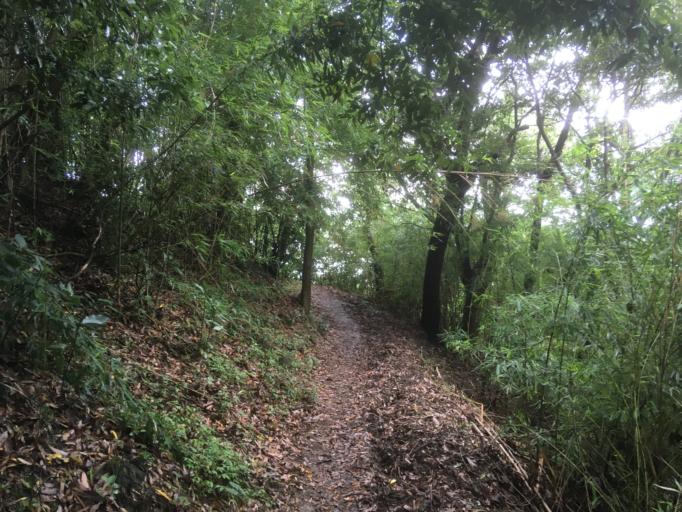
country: JP
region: Nara
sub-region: Ikoma-shi
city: Ikoma
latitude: 34.6673
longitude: 135.6725
